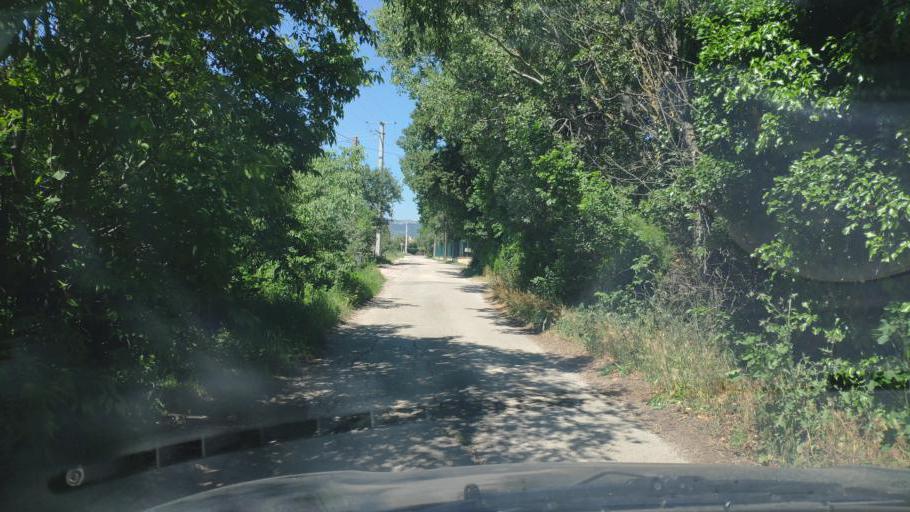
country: FR
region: Provence-Alpes-Cote d'Azur
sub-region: Departement du Vaucluse
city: Carpentras
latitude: 44.0829
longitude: 5.0565
